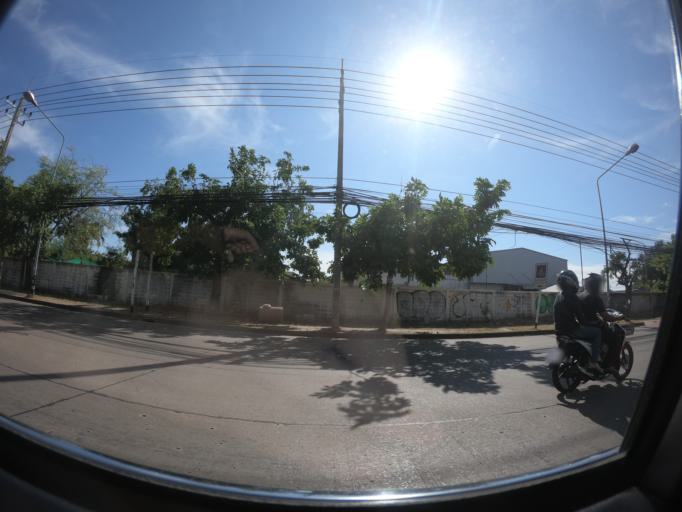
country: TH
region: Khon Kaen
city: Khon Kaen
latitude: 16.4170
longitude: 102.8195
